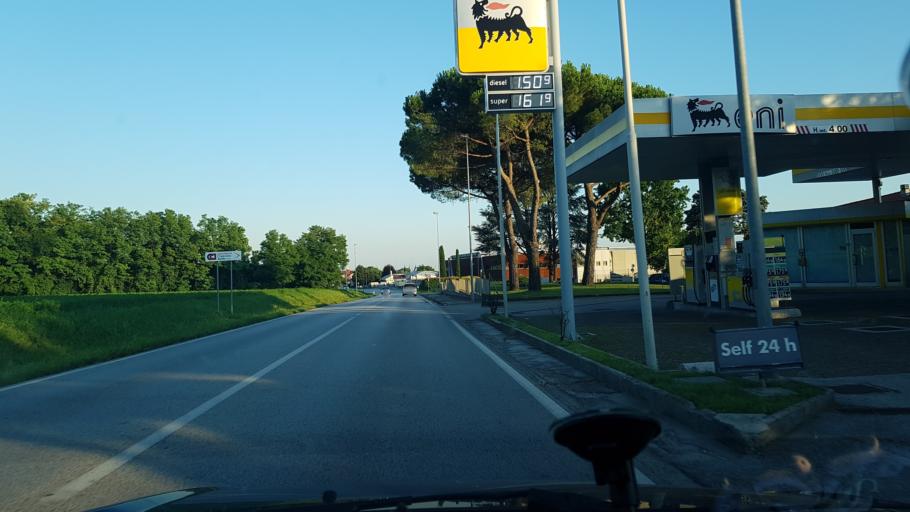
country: IT
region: Friuli Venezia Giulia
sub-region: Provincia di Udine
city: Fagagna
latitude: 46.1051
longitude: 13.0936
